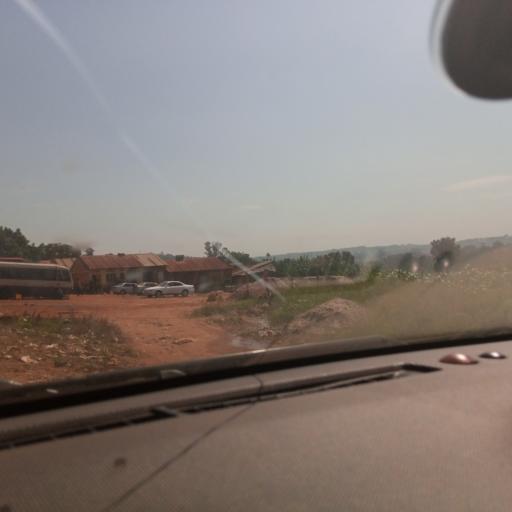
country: UG
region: Central Region
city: Masaka
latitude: -0.3455
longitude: 31.7411
